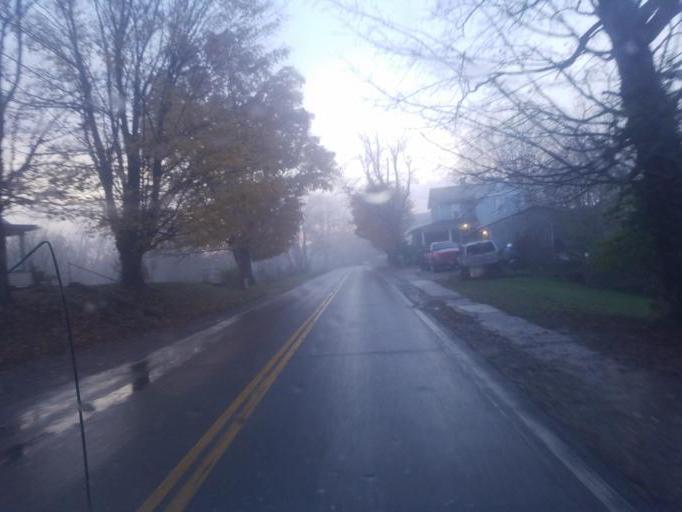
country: US
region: Ohio
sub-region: Morgan County
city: McConnelsville
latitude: 39.4939
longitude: -81.8653
